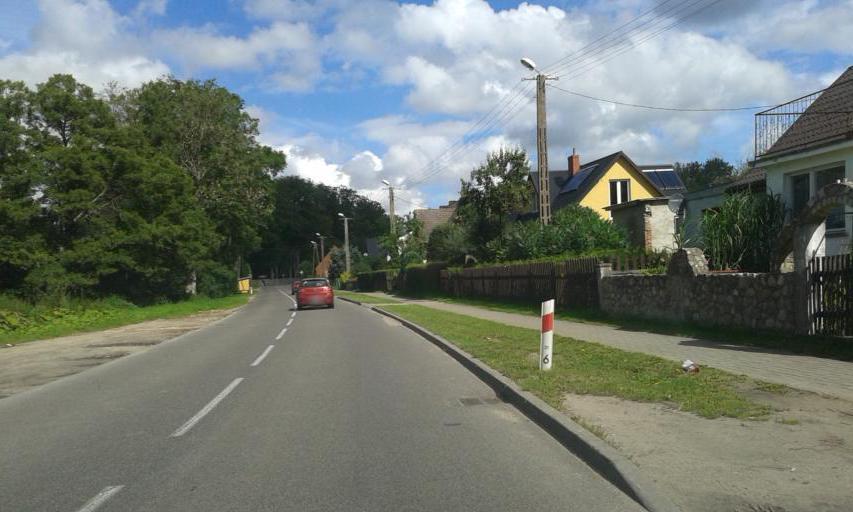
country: PL
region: West Pomeranian Voivodeship
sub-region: Powiat koszalinski
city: Polanow
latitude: 54.2110
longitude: 16.7022
